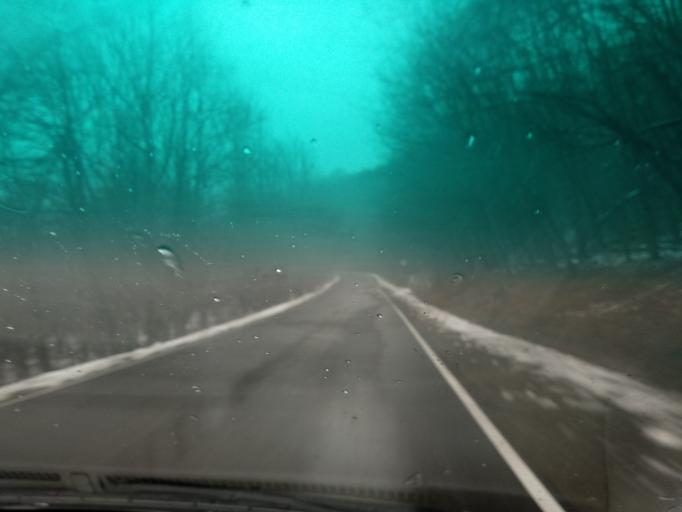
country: RU
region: Krasnodarskiy
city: Khadyzhensk
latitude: 44.2663
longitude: 39.3501
